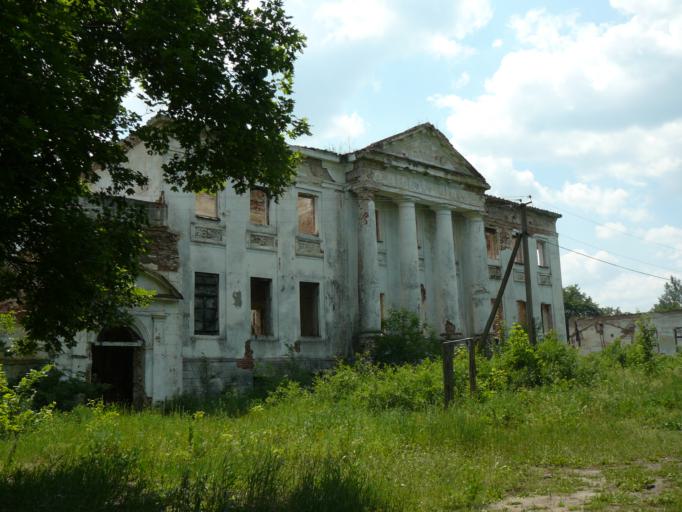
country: RU
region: Penza
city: Tamala
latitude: 52.3920
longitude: 43.3800
